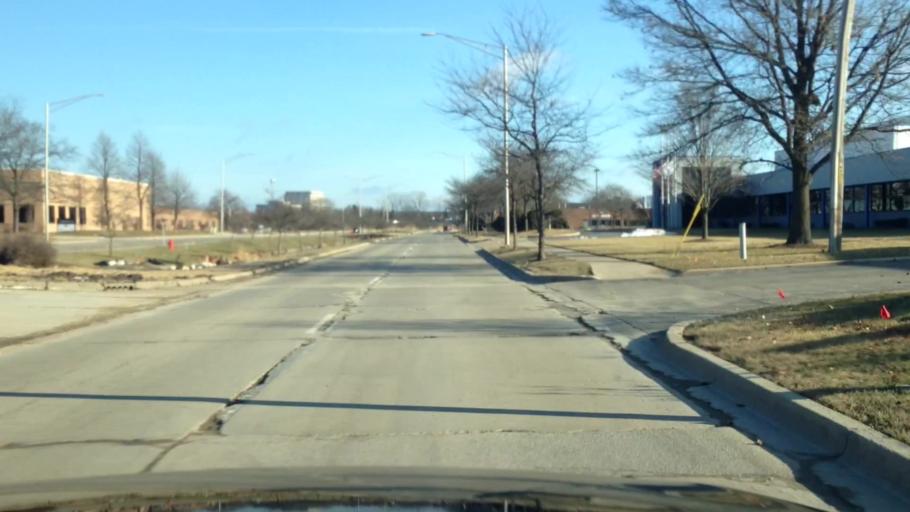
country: US
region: Illinois
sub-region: Cook County
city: Hoffman Estates
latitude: 42.0560
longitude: -88.0576
